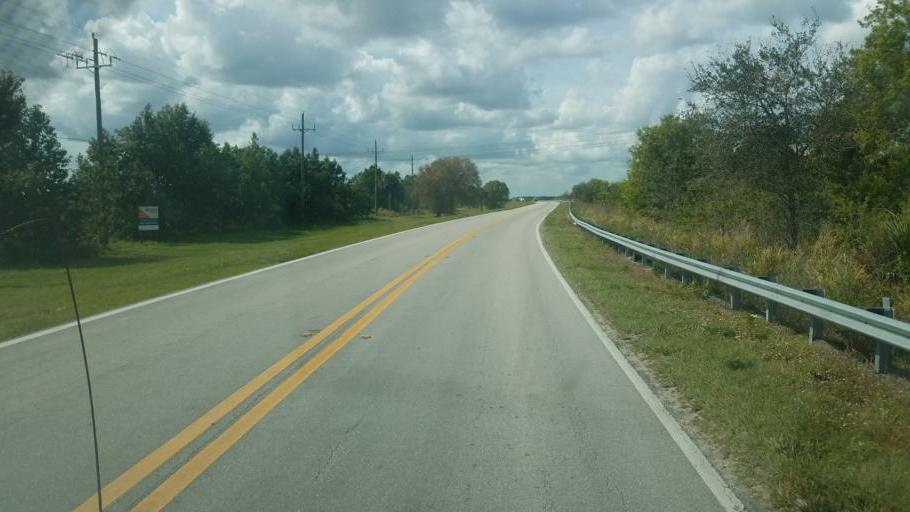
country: US
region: Florida
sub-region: Saint Lucie County
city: Lakewood Park
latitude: 27.4475
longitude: -80.5427
